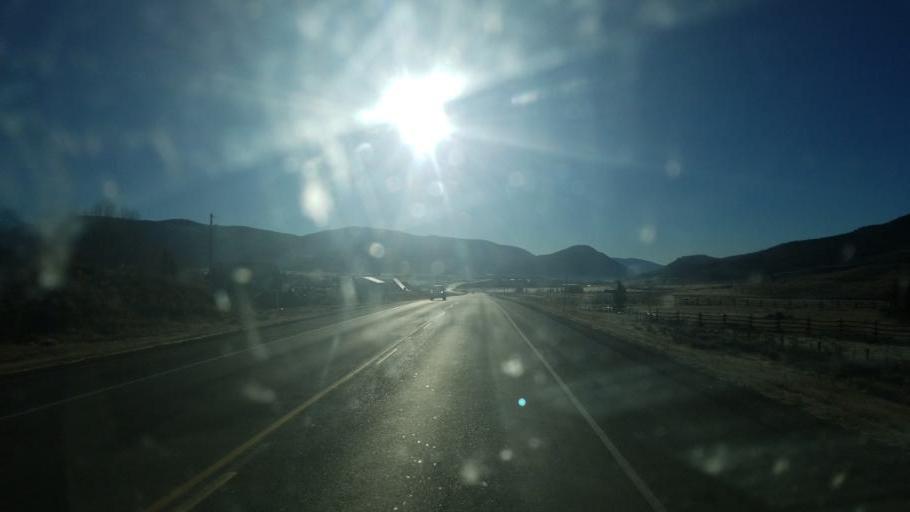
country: US
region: Colorado
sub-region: Gunnison County
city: Crested Butte
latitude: 38.8593
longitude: -106.9690
